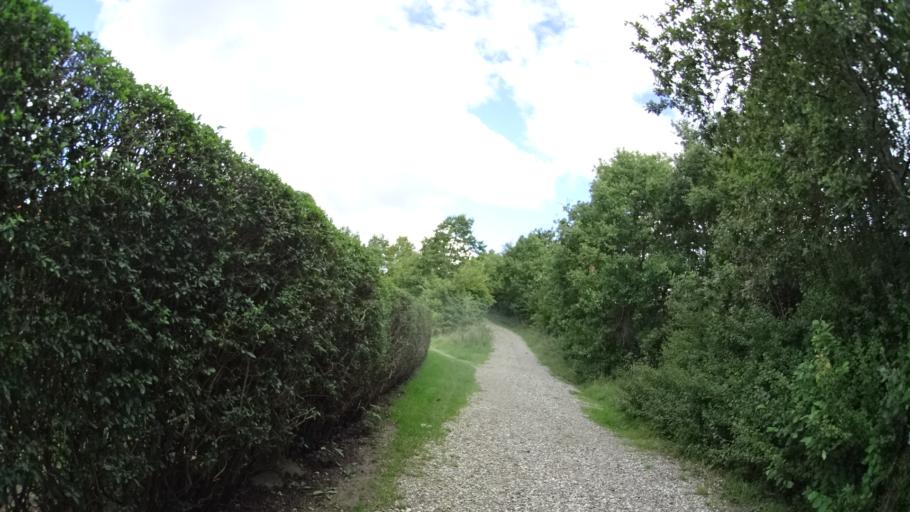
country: DK
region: Central Jutland
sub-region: Arhus Kommune
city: Arhus
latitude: 56.1129
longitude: 10.1895
